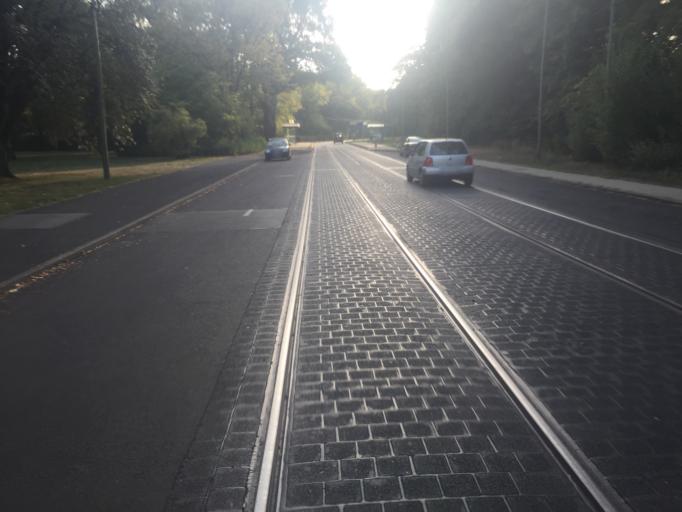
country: DE
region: Hesse
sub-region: Regierungsbezirk Kassel
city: Baunatal
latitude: 51.3106
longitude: 9.4290
